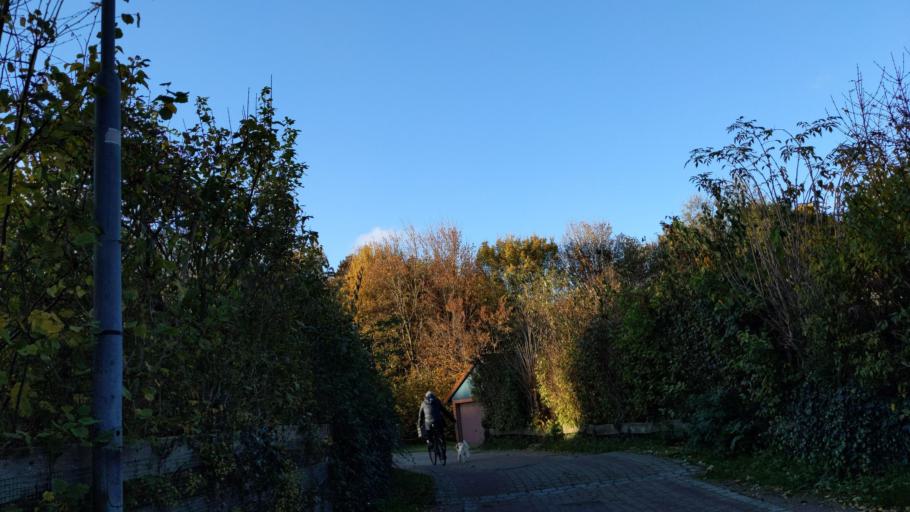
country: DE
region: Schleswig-Holstein
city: Sierksdorf
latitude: 54.0707
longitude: 10.7787
